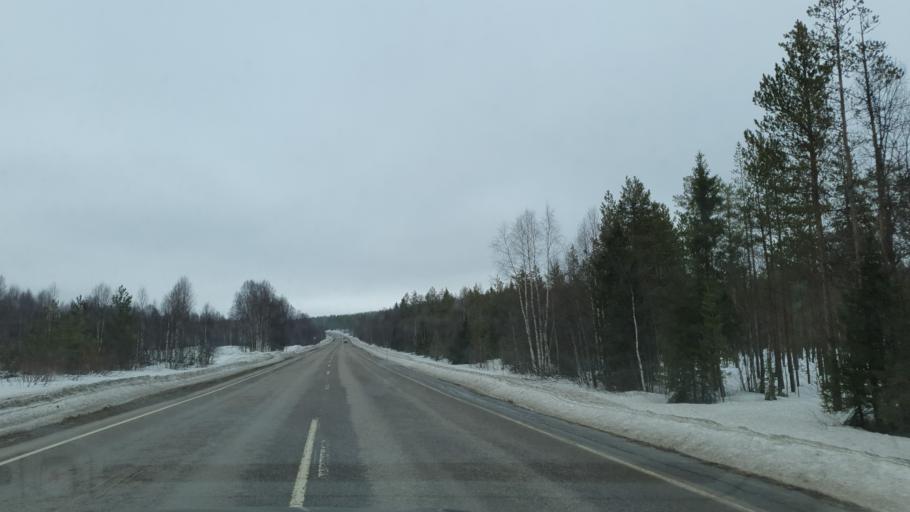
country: FI
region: Lapland
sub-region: Torniolaakso
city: Pello
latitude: 66.8719
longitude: 24.0552
